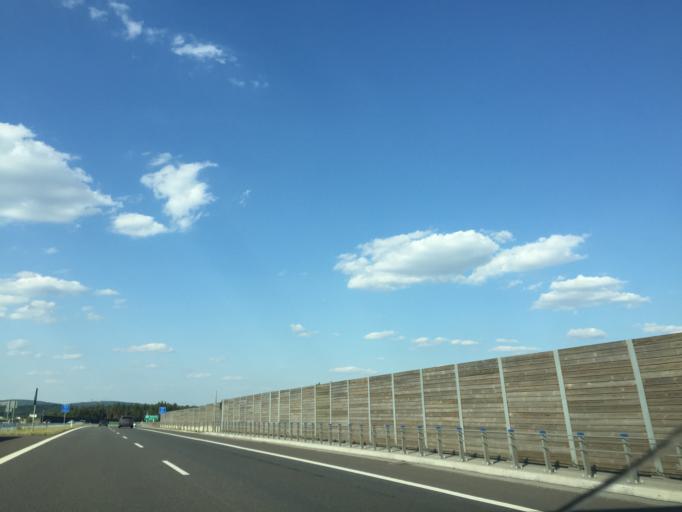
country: PL
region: Swietokrzyskie
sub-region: Powiat jedrzejowski
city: Sobkow
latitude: 50.7420
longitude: 20.4140
